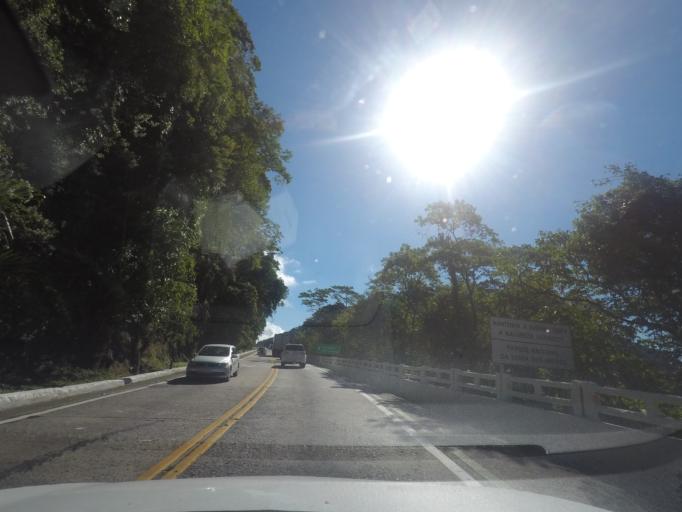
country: BR
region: Rio de Janeiro
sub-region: Teresopolis
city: Teresopolis
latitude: -22.4637
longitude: -42.9903
